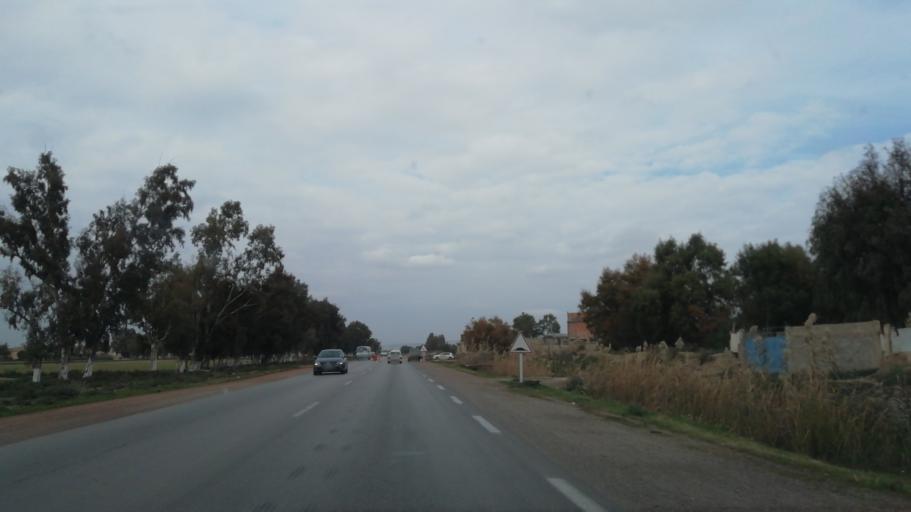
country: DZ
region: Mostaganem
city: Mostaganem
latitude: 35.6826
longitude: 0.0567
